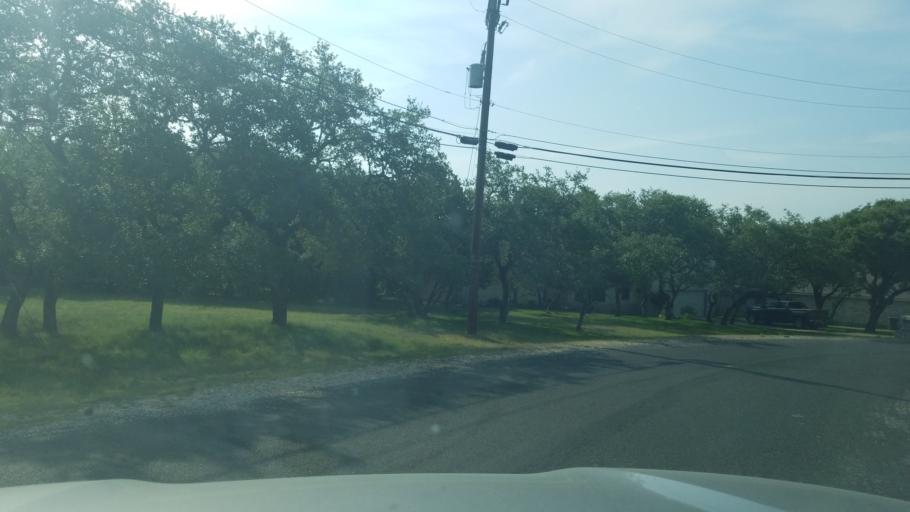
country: US
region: Texas
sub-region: Bexar County
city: Timberwood Park
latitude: 29.6999
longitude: -98.4939
